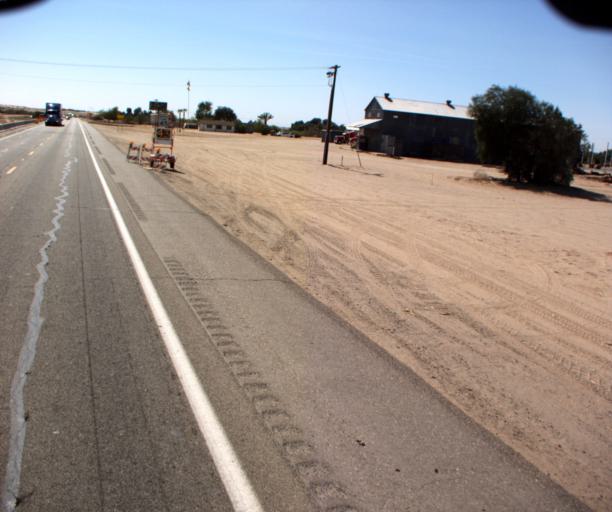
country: US
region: Arizona
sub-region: Yuma County
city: Fortuna Foothills
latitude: 32.7082
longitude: -114.4322
